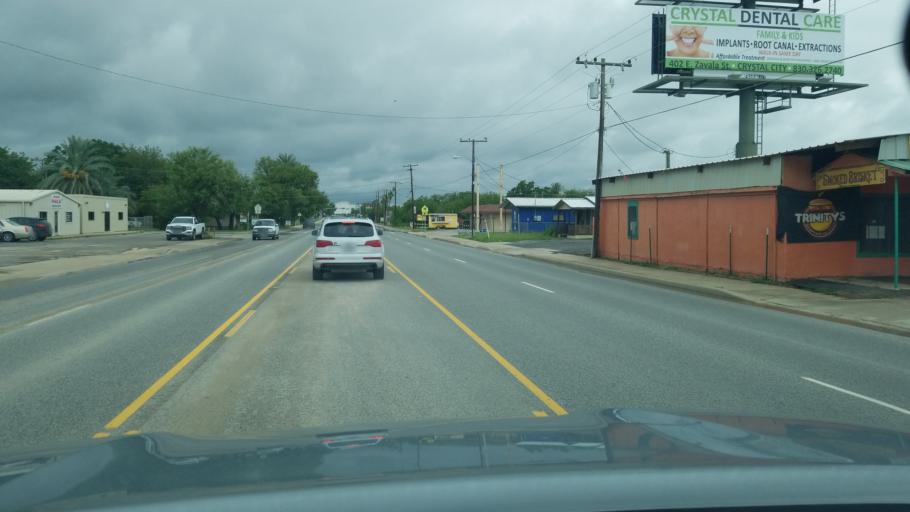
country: US
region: Texas
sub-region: Dimmit County
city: Carrizo Springs
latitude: 28.5248
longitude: -99.8557
